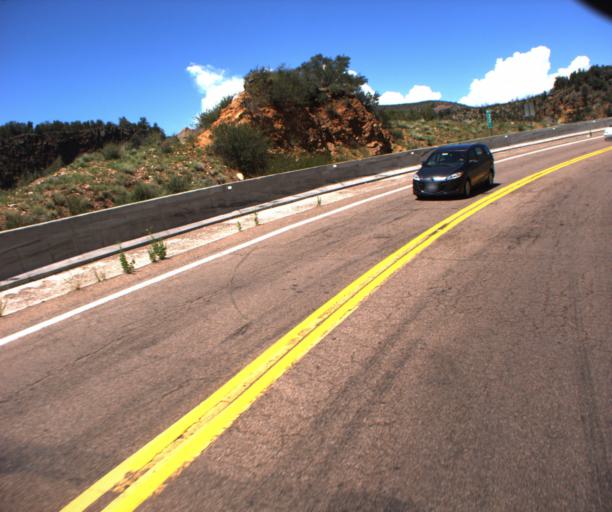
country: US
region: Arizona
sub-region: Navajo County
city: Cibecue
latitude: 34.0363
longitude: -110.2410
